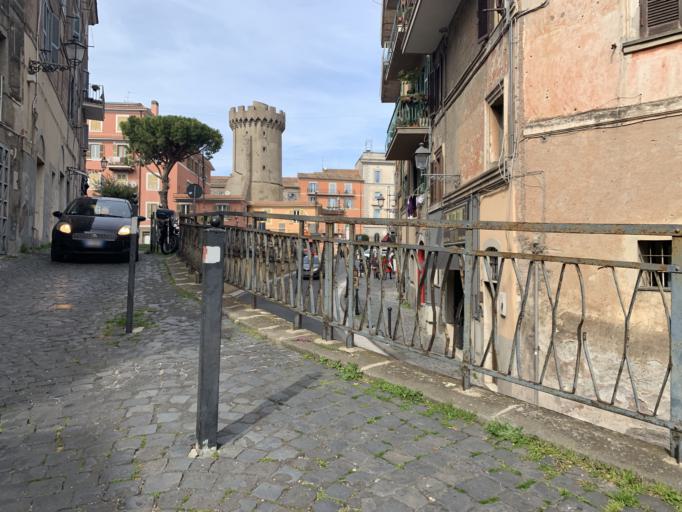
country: IT
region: Latium
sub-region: Citta metropolitana di Roma Capitale
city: Castel Gandolfo
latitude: 41.7682
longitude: 12.6617
